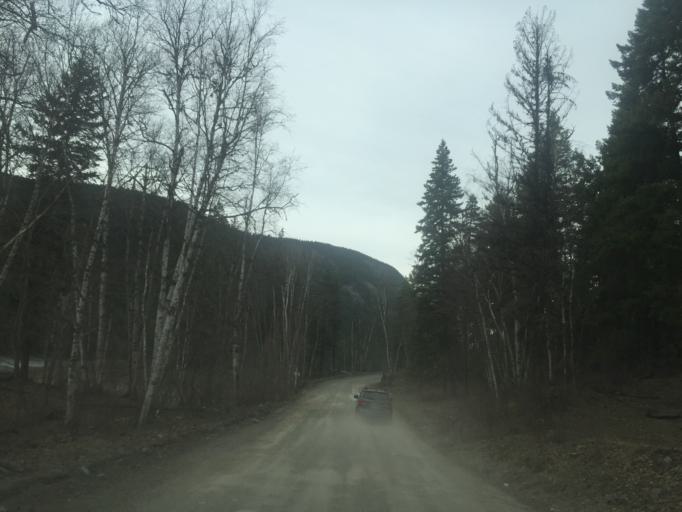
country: CA
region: British Columbia
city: Chase
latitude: 51.3870
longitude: -120.1256
